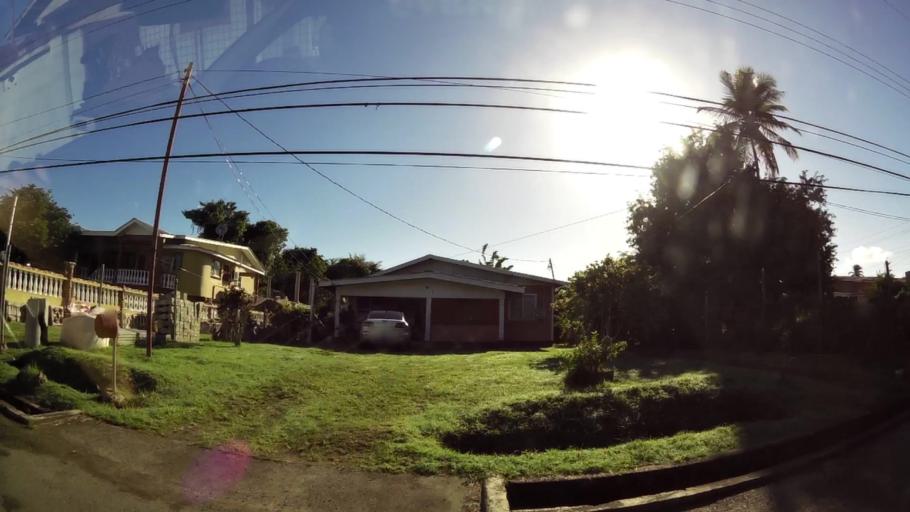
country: TT
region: Tobago
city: Scarborough
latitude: 11.1535
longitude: -60.8236
